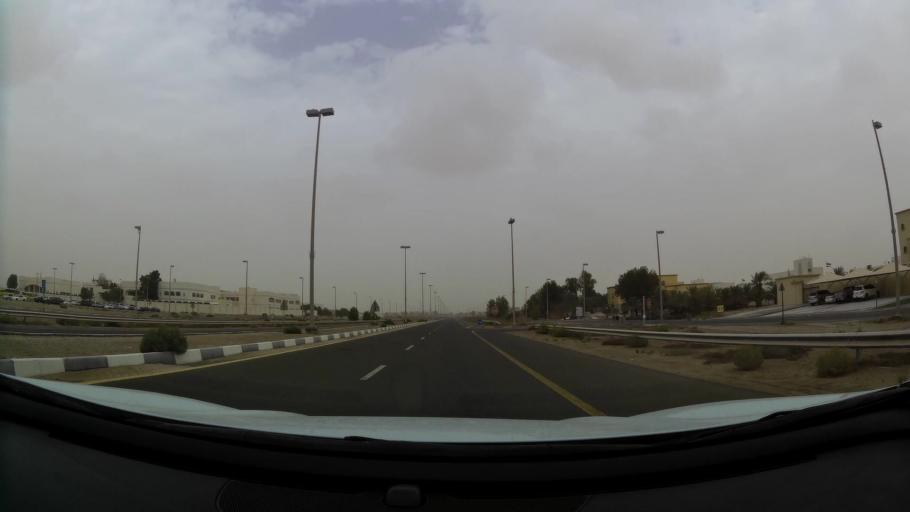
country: AE
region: Abu Dhabi
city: Abu Dhabi
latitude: 24.4055
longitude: 54.7341
